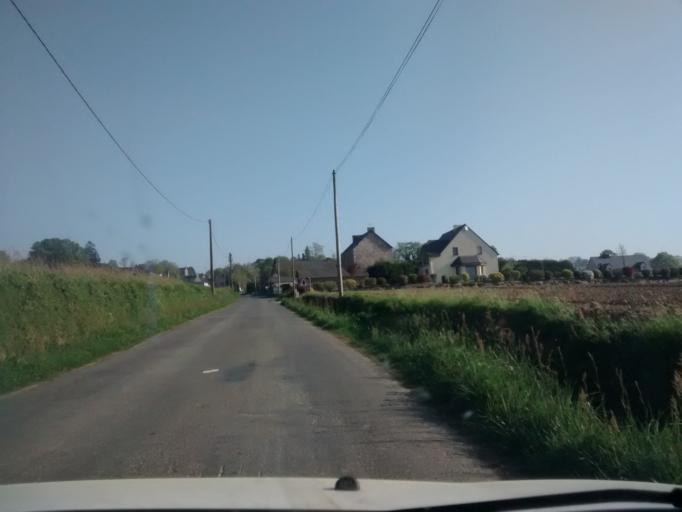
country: FR
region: Brittany
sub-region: Departement d'Ille-et-Vilaine
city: Saint-Sauveur-des-Landes
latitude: 48.3100
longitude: -1.3088
